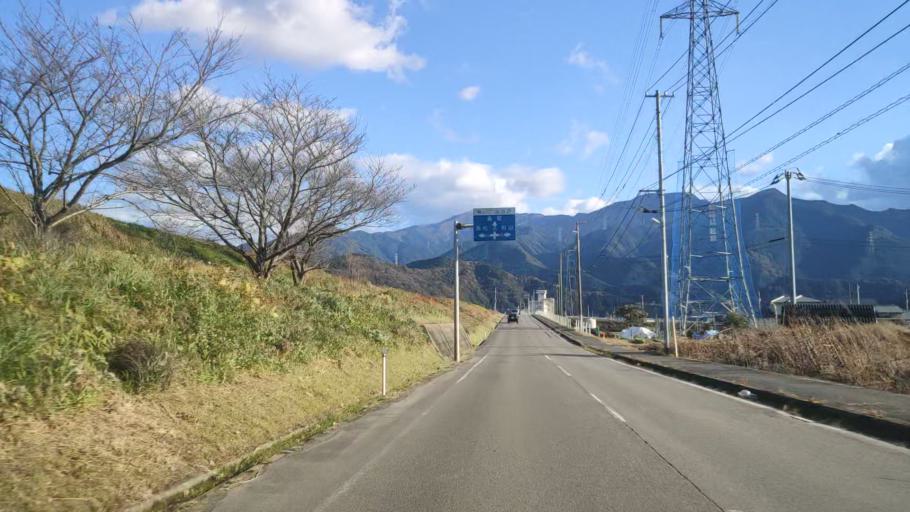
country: JP
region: Ehime
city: Saijo
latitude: 33.9048
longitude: 133.1793
